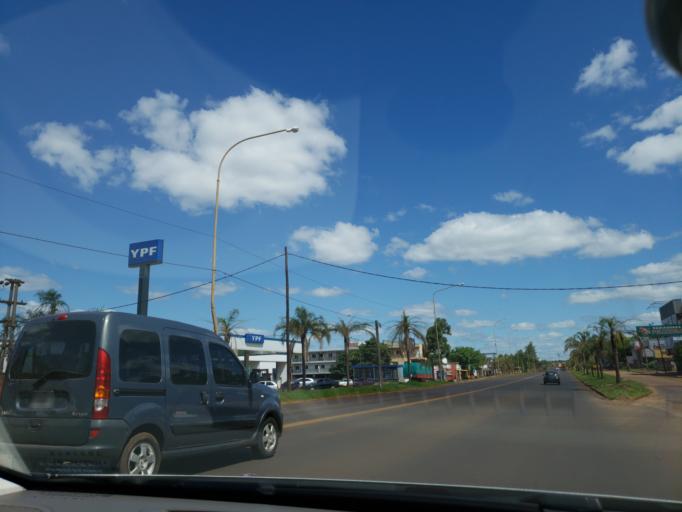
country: AR
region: Misiones
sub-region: Departamento de Capital
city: Posadas
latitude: -27.4086
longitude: -55.9025
